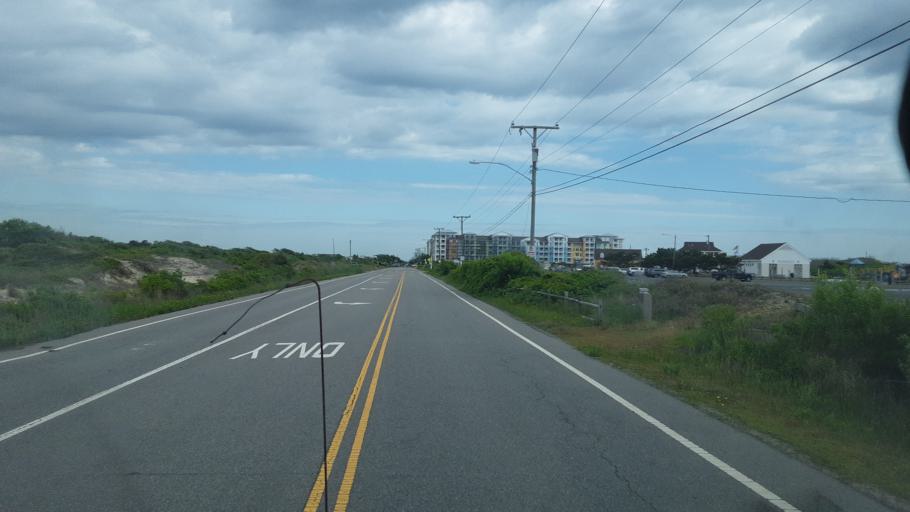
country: US
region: Virginia
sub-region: City of Virginia Beach
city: Virginia Beach
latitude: 36.6918
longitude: -75.9245
